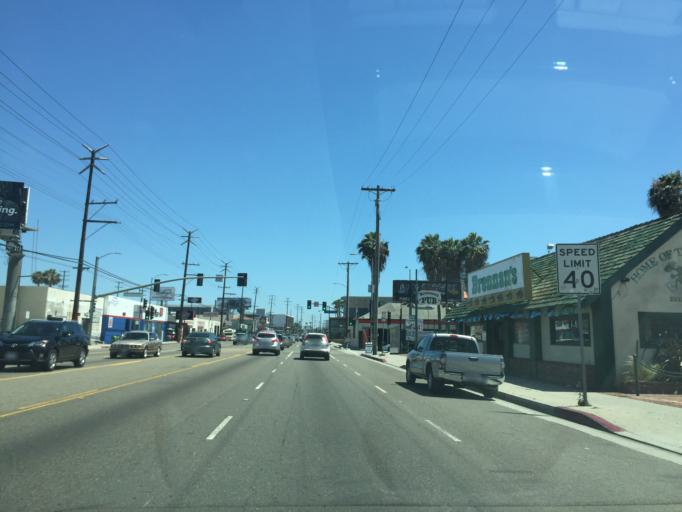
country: US
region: California
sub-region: Los Angeles County
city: Marina del Rey
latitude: 33.9887
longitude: -118.4462
